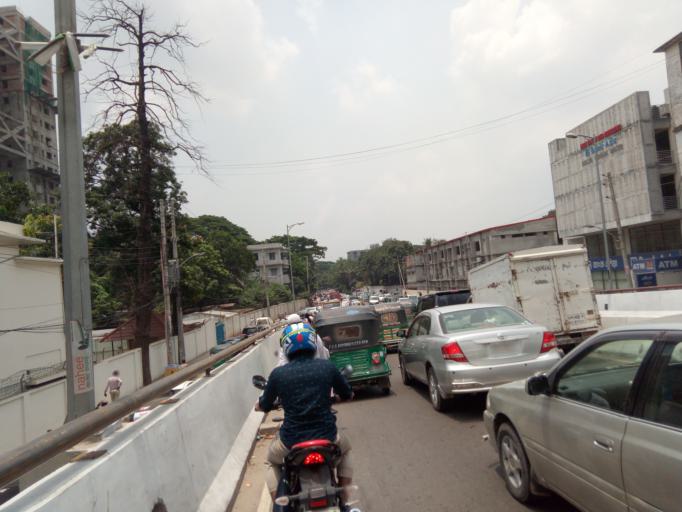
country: BD
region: Dhaka
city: Paltan
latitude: 23.7474
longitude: 90.4040
